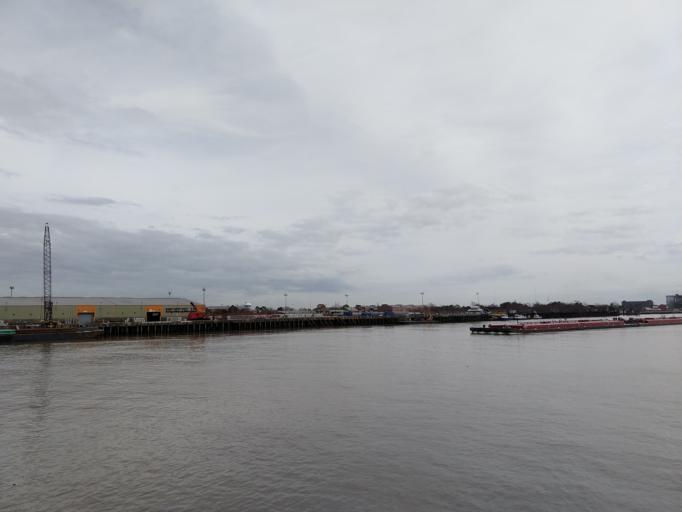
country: US
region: Louisiana
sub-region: Saint Bernard Parish
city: Arabi
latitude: 29.9510
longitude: -90.0194
